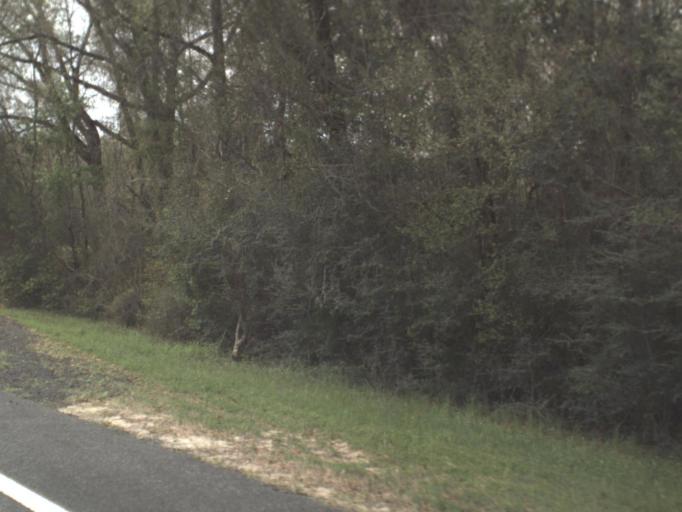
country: US
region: Florida
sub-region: Calhoun County
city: Blountstown
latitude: 30.5574
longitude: -85.1854
